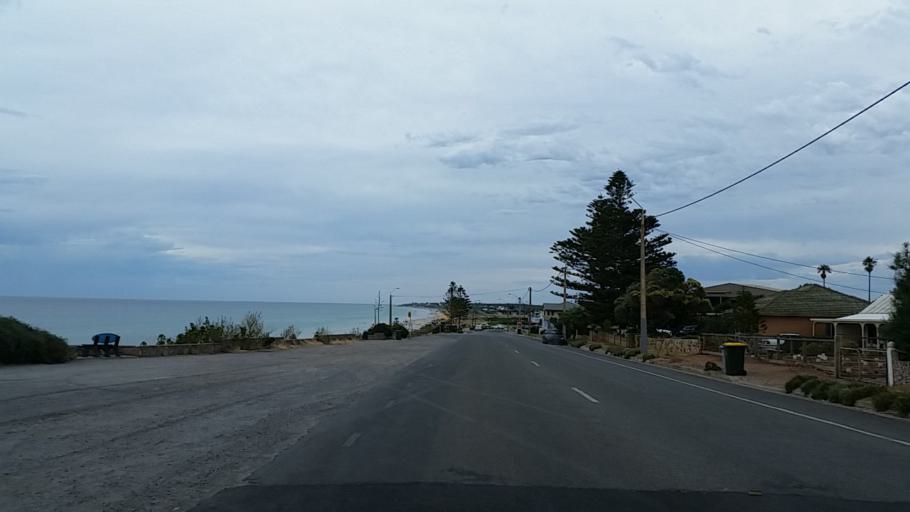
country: AU
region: South Australia
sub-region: Onkaparinga
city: Port Willunga
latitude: -35.3316
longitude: 138.4481
